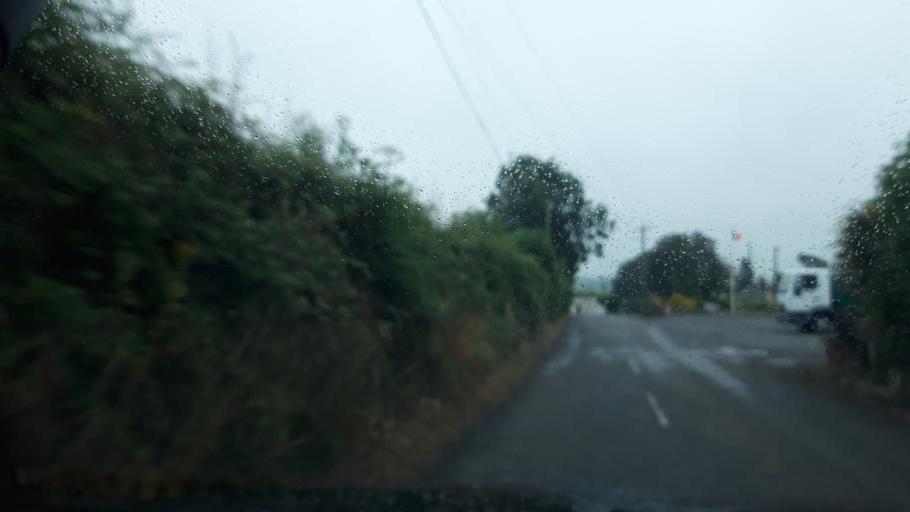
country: IE
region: Leinster
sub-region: Kilkenny
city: Callan
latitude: 52.6279
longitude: -7.5475
